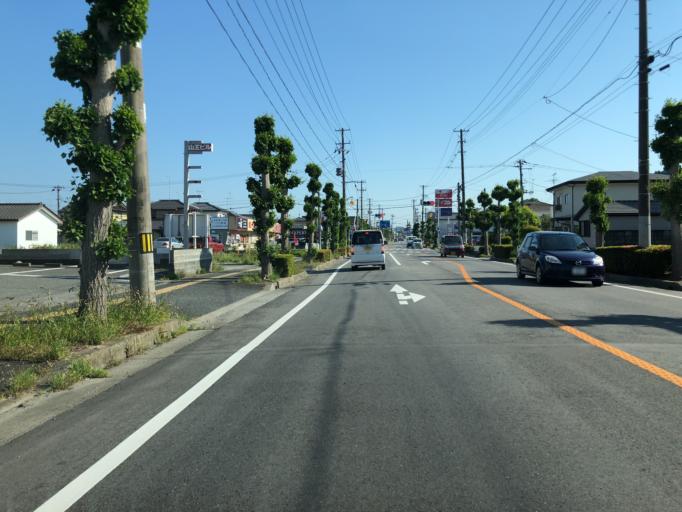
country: JP
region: Ibaraki
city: Kitaibaraki
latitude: 36.9145
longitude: 140.7749
